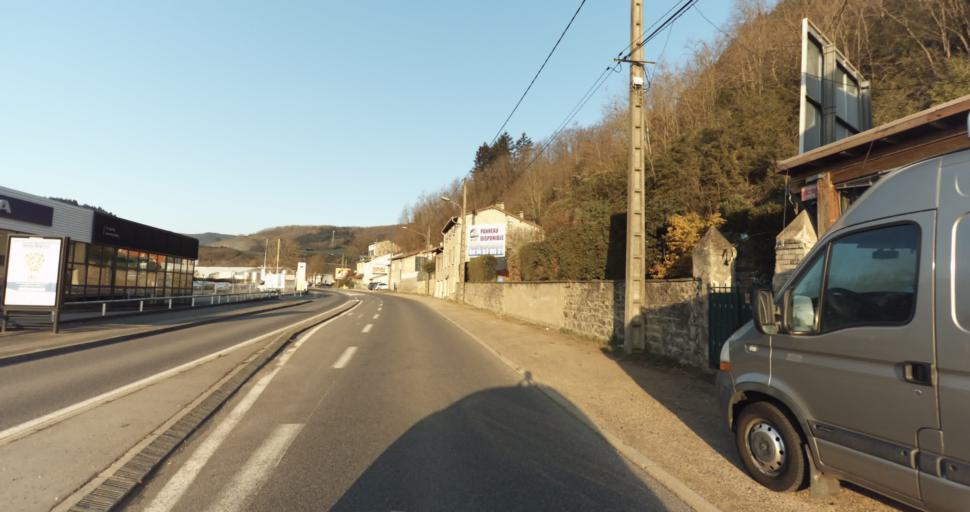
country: FR
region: Rhone-Alpes
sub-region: Departement du Rhone
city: Tarare
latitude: 45.8963
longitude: 4.4174
